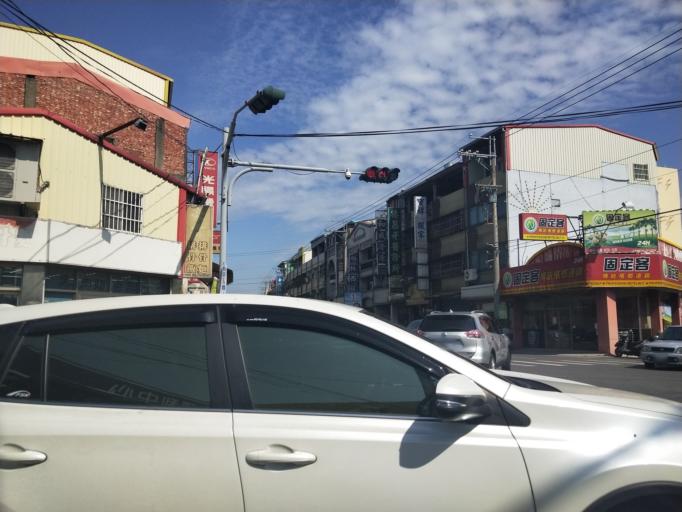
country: TW
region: Taiwan
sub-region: Changhua
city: Chang-hua
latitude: 24.0618
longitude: 120.5173
